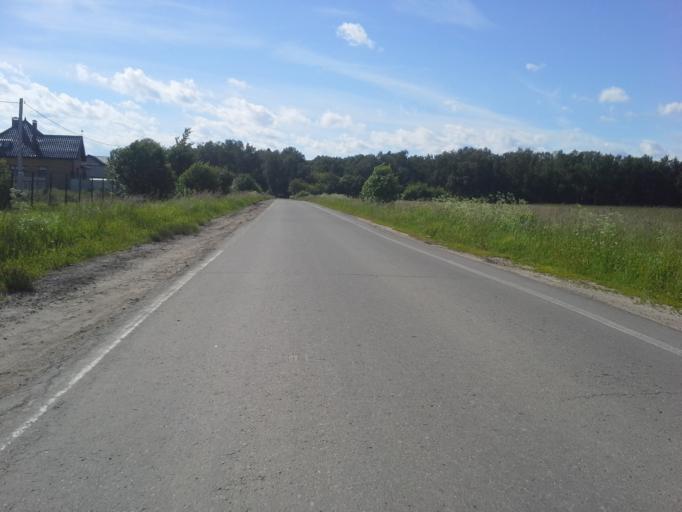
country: RU
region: Moskovskaya
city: Dubrovitsy
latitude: 55.4555
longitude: 37.4416
